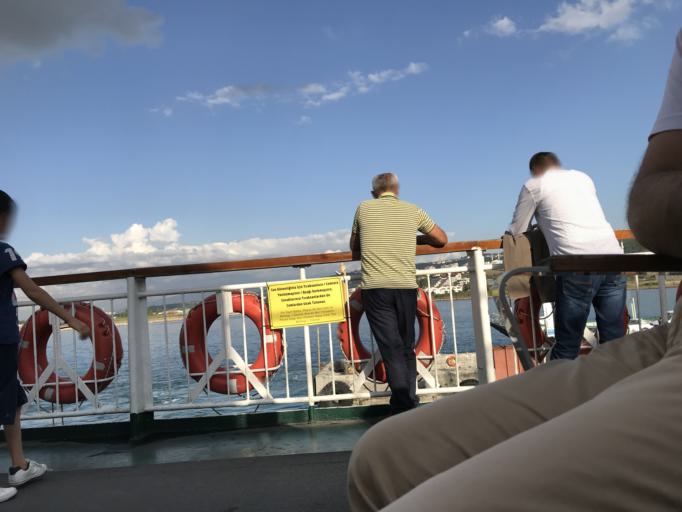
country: TR
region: Yalova
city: Taskopru
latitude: 40.6919
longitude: 29.4344
